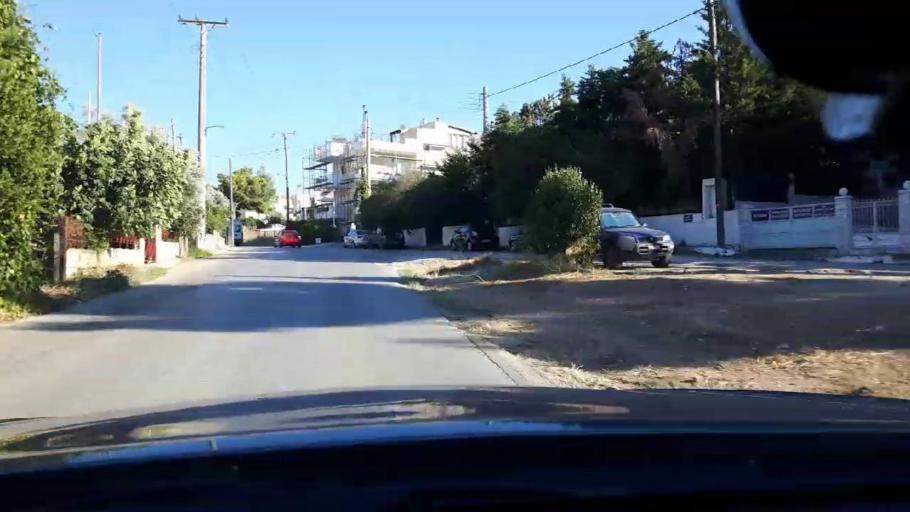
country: GR
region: Attica
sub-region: Nomarchia Anatolikis Attikis
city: Limin Mesoyaias
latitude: 37.8783
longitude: 24.0059
